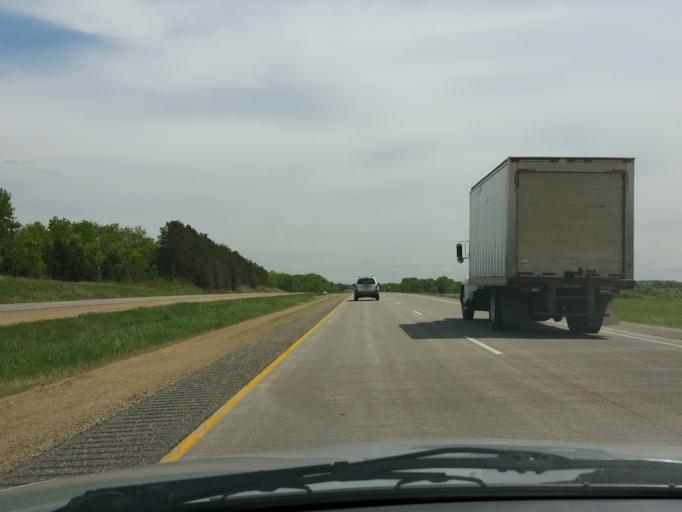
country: US
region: Wisconsin
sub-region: Pierce County
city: River Falls
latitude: 44.9263
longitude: -92.6792
